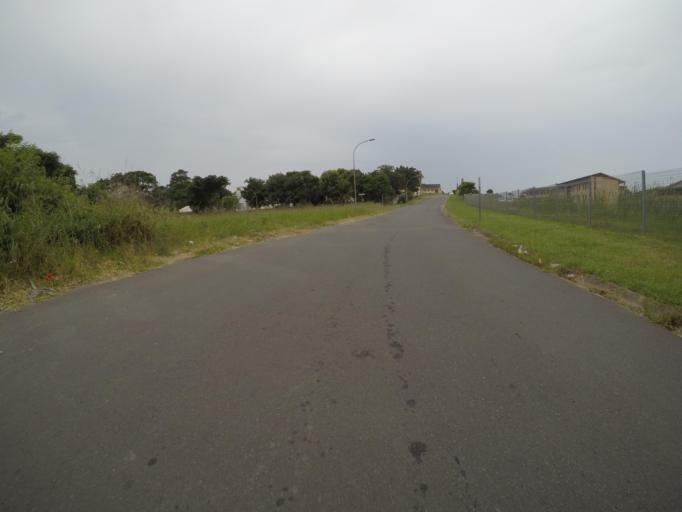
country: ZA
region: Eastern Cape
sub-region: Buffalo City Metropolitan Municipality
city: East London
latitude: -32.9986
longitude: 27.8569
